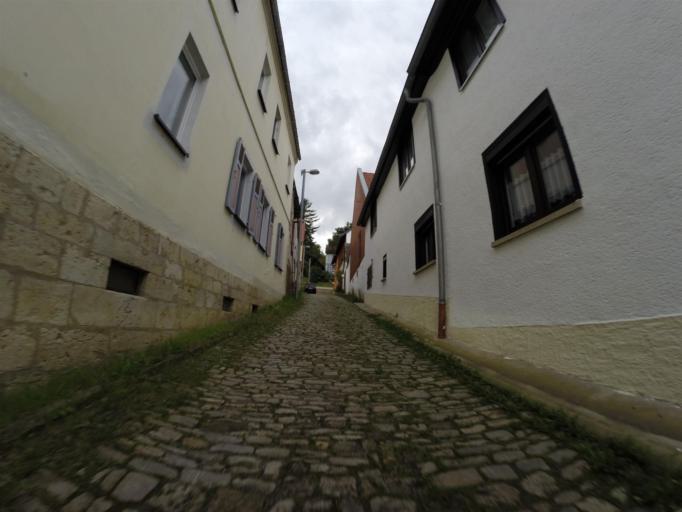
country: DE
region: Thuringia
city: Jena
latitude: 50.9591
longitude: 11.6142
